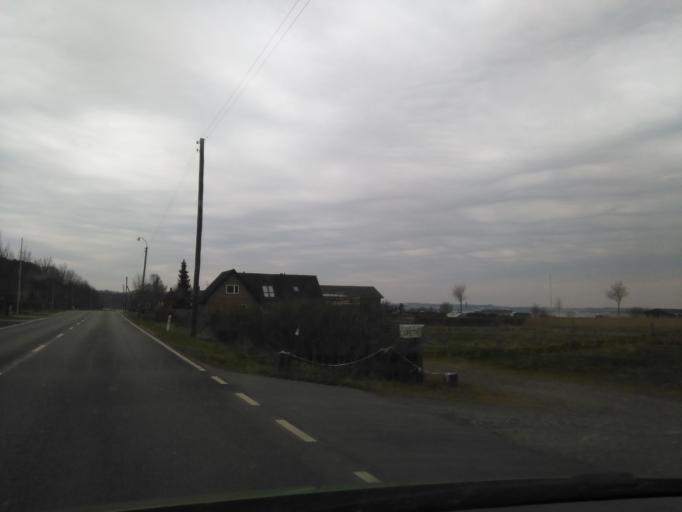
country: DK
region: North Denmark
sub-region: Mariagerfjord Kommune
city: Hadsund
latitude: 56.7039
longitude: 10.1155
